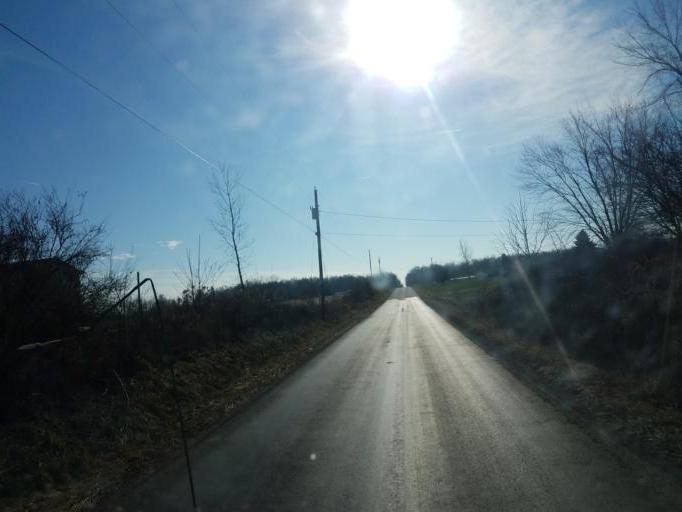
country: US
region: Ohio
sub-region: Morrow County
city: Cardington
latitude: 40.4946
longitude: -82.8678
